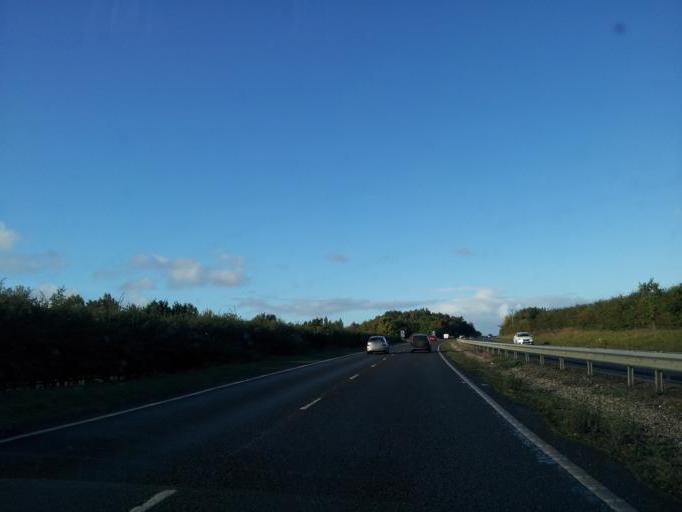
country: GB
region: England
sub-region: Norfolk
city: Swaffham
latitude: 52.6536
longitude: 0.6684
